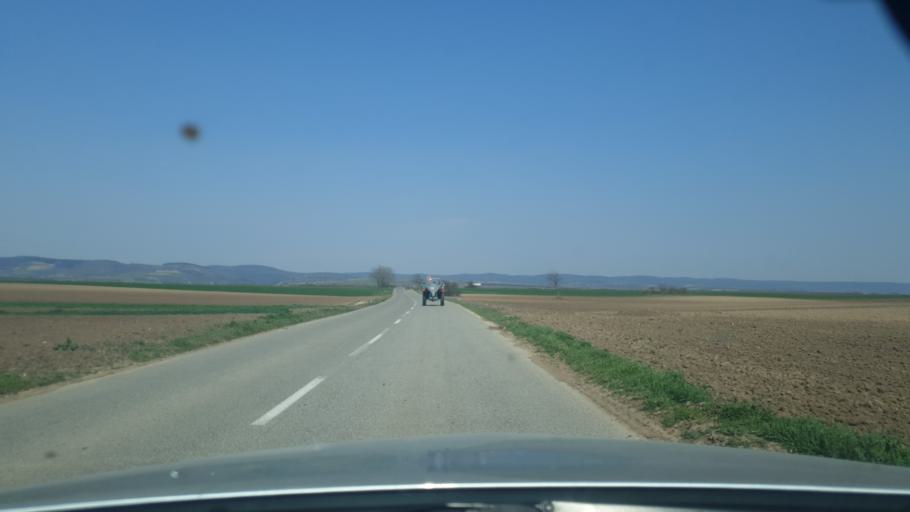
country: RS
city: Vrdnik
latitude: 45.0605
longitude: 19.7682
